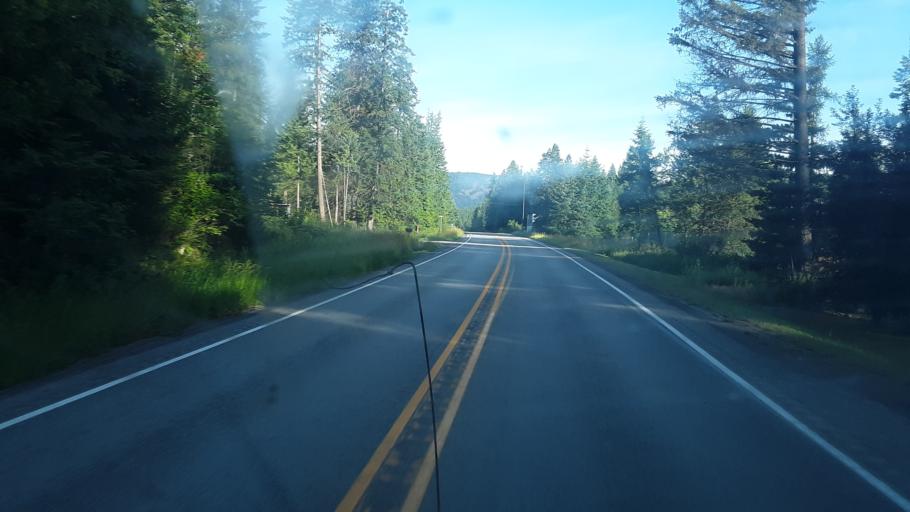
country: US
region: Idaho
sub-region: Boundary County
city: Bonners Ferry
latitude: 48.6023
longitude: -116.0049
